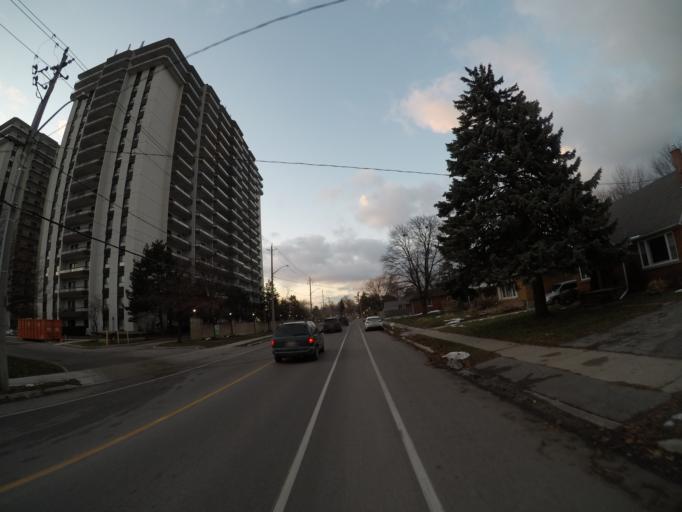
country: CA
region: Ontario
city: Waterloo
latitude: 43.4641
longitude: -80.4952
